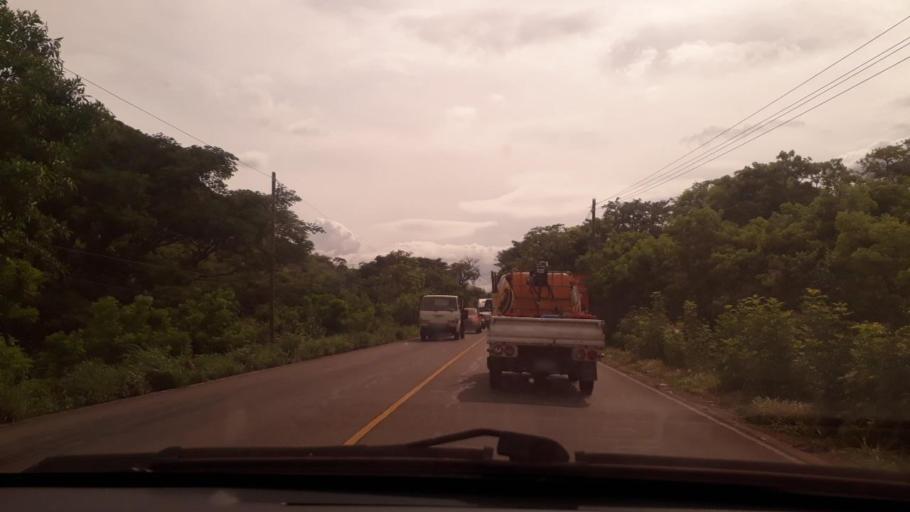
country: GT
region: Jutiapa
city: Jutiapa
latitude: 14.3013
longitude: -89.8747
